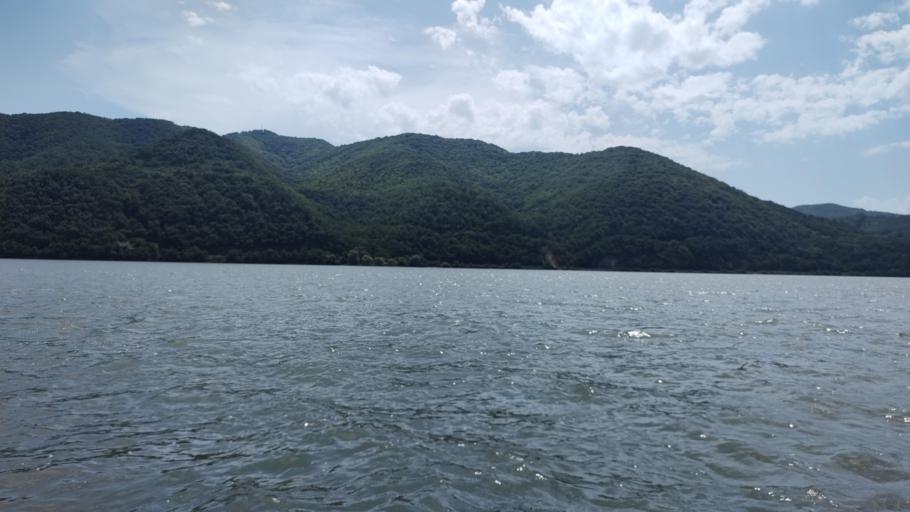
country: RO
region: Caras-Severin
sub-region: Comuna Berzasca
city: Liubcova
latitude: 44.6477
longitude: 21.8991
